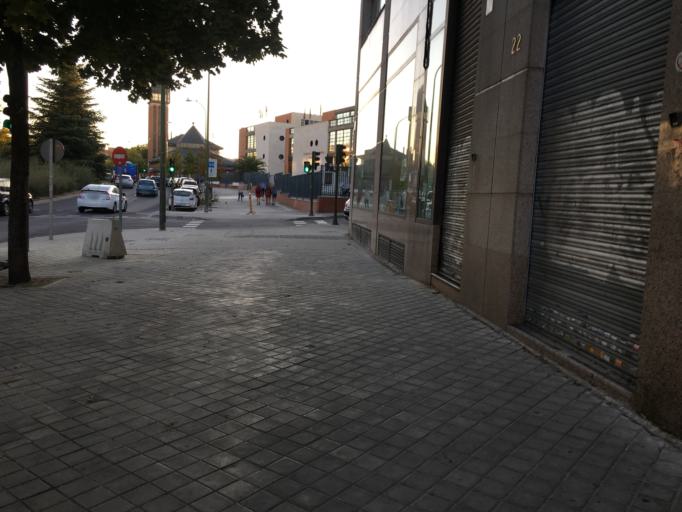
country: ES
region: Madrid
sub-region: Provincia de Madrid
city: Moratalaz
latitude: 40.4296
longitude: -3.6427
